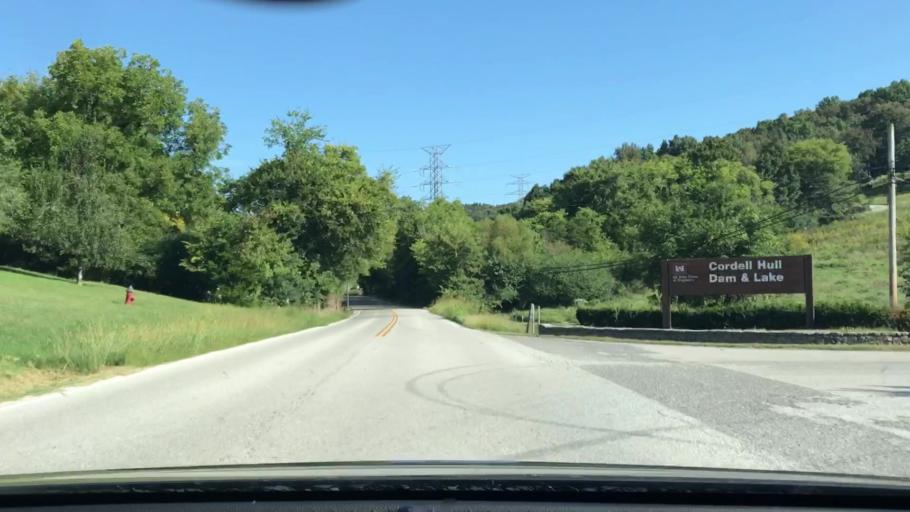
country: US
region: Tennessee
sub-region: Smith County
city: Carthage
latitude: 36.2814
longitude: -85.9465
